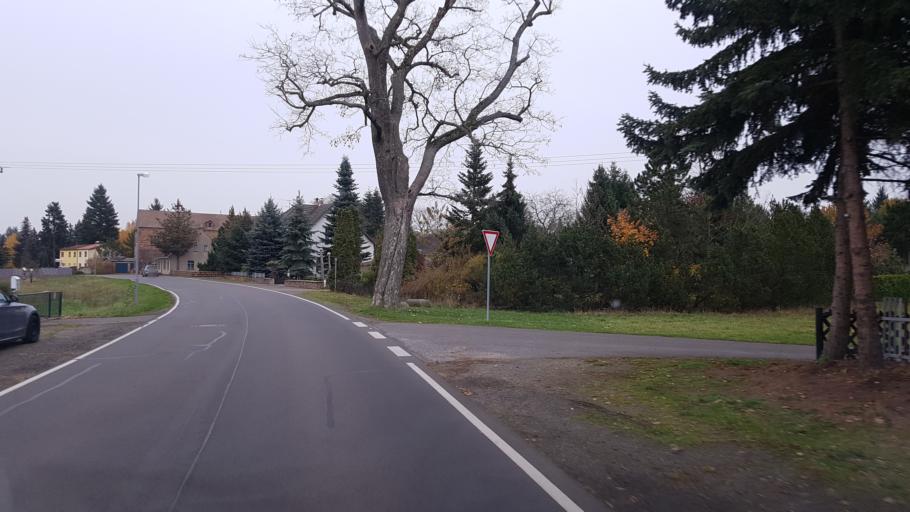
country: DE
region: Brandenburg
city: Crinitz
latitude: 51.7372
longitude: 13.7532
